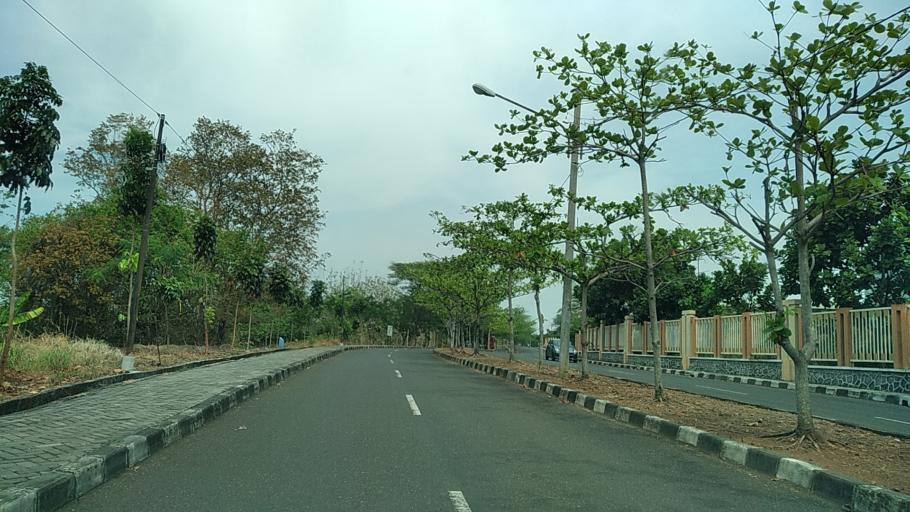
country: ID
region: Central Java
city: Semarang
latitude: -7.0461
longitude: 110.4425
